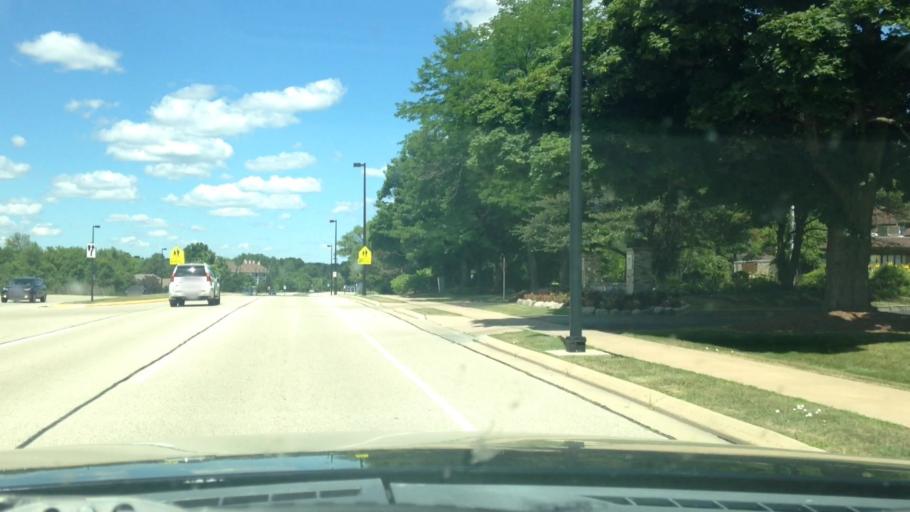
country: US
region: Wisconsin
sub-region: Waukesha County
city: Butler
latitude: 43.1501
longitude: -88.0766
